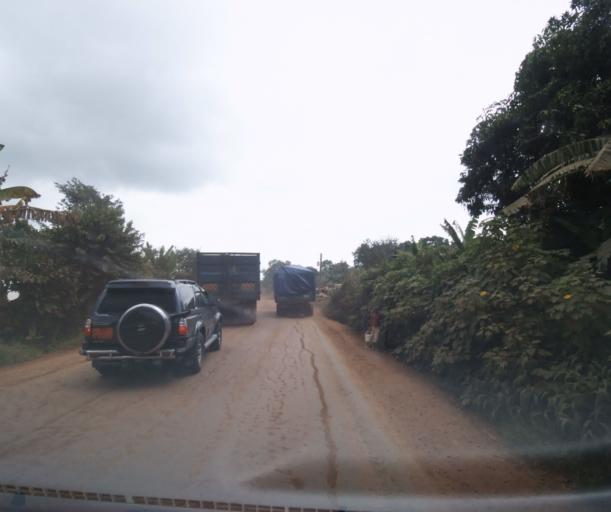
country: CM
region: West
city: Mbouda
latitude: 5.6675
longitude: 10.2190
